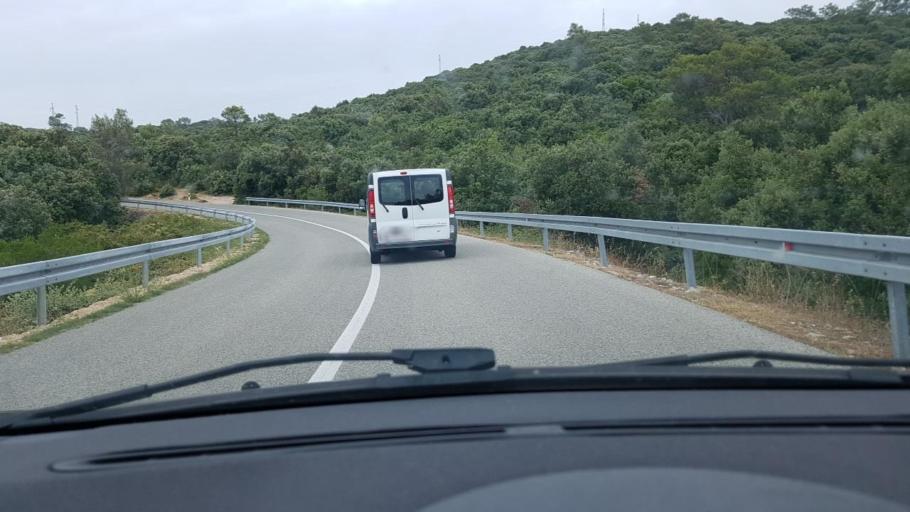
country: HR
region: Dubrovacko-Neretvanska
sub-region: Grad Korcula
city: Zrnovo
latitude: 42.9431
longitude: 17.0075
